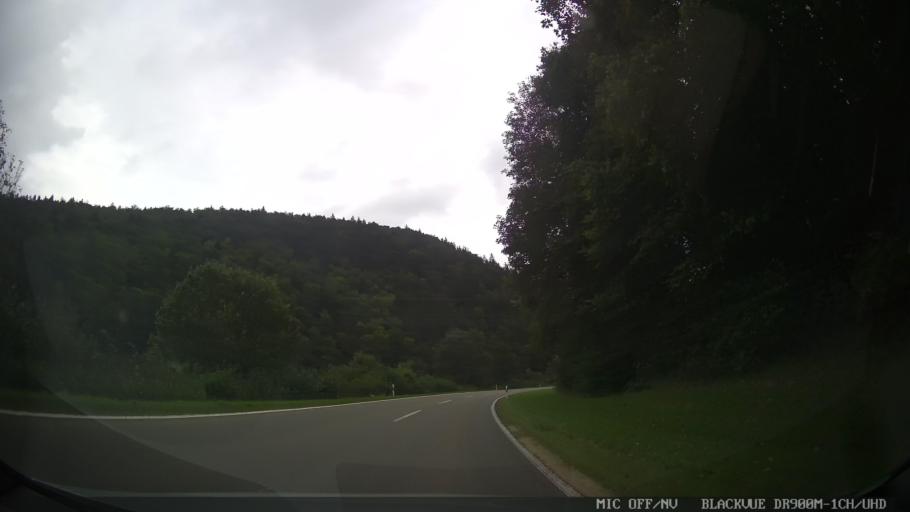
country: DE
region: Baden-Wuerttemberg
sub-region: Freiburg Region
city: Barenthal
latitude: 48.0586
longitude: 8.9320
